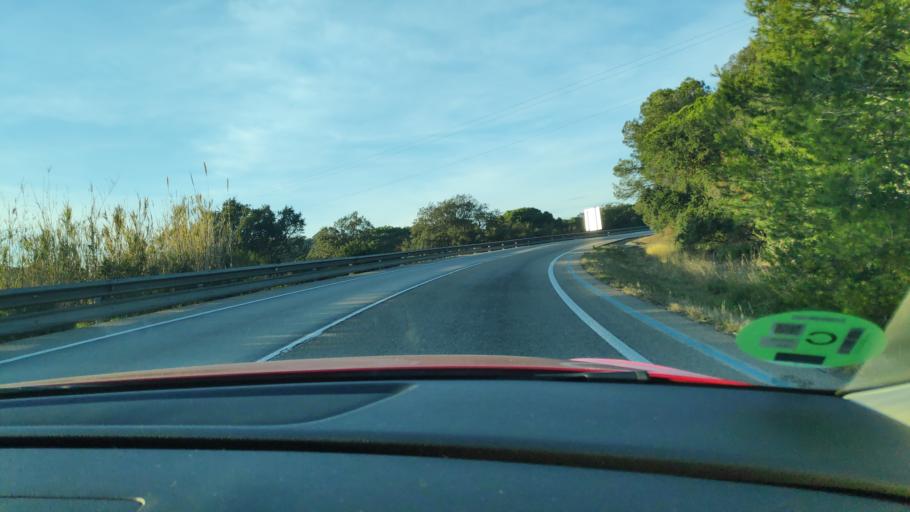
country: ES
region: Catalonia
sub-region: Provincia de Girona
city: Lloret de Mar
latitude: 41.7184
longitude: 2.8262
